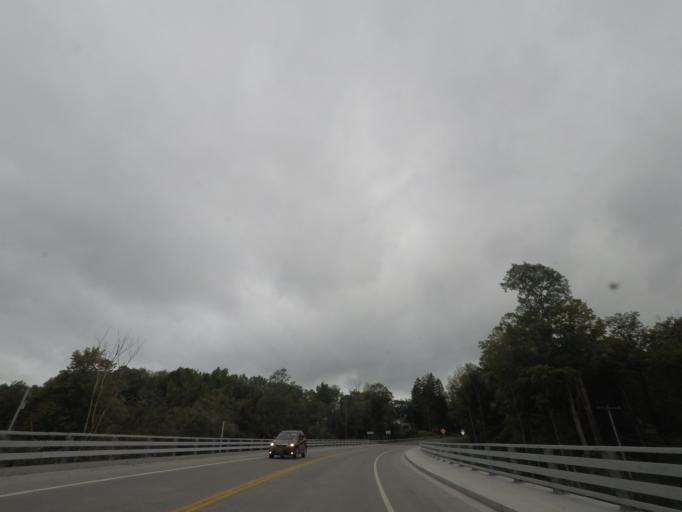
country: US
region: New York
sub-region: Rensselaer County
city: Hoosick Falls
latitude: 42.9269
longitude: -73.3440
